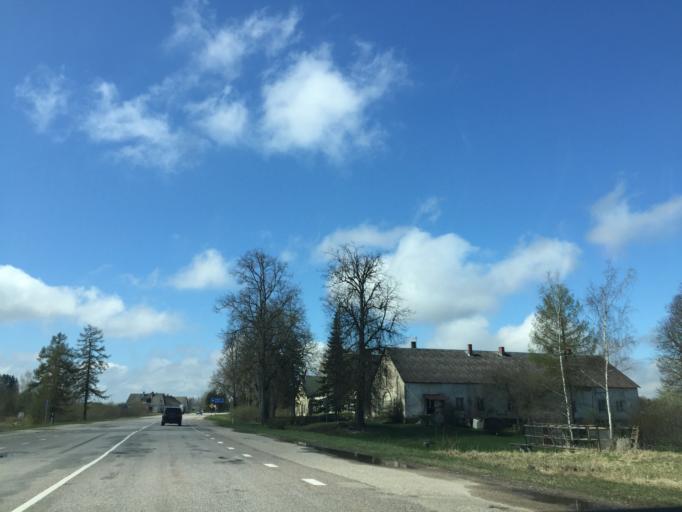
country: LV
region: Apes Novads
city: Ape
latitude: 57.4771
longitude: 26.5324
